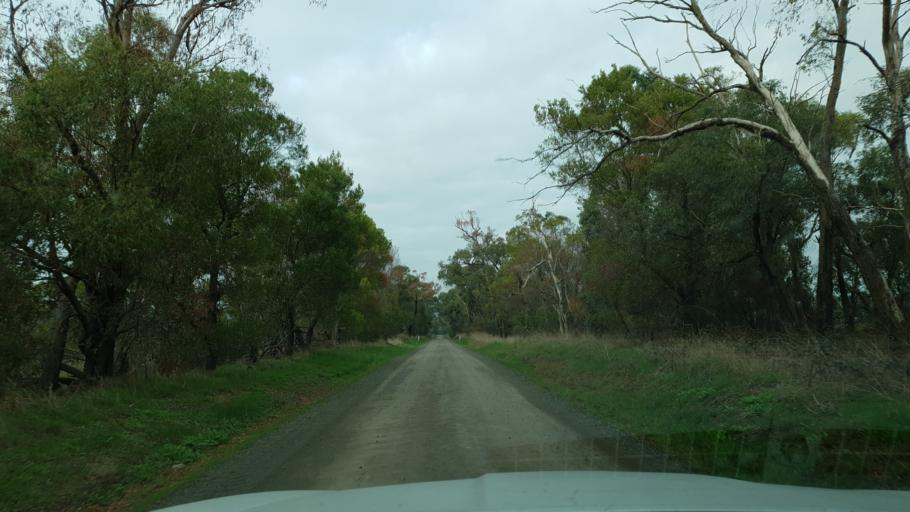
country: AU
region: Victoria
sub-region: Latrobe
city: Moe
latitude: -38.1689
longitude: 146.1313
